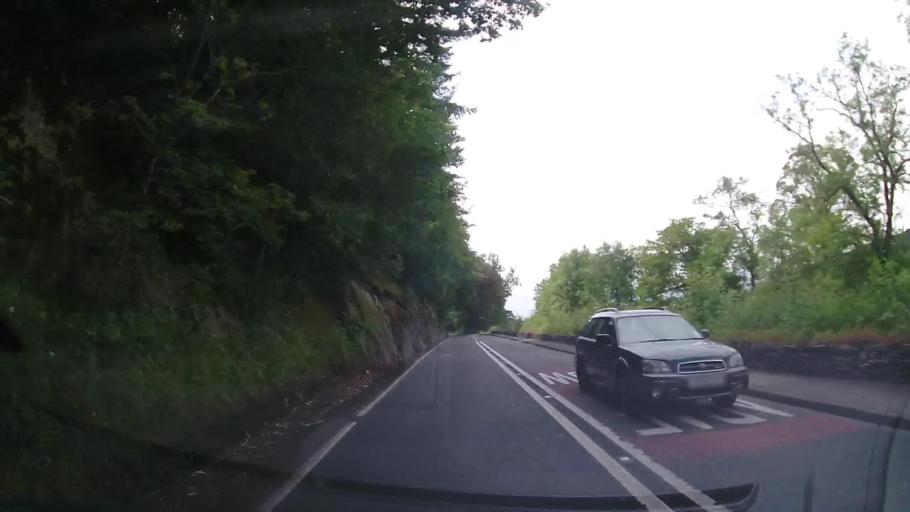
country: GB
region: Wales
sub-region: Denbighshire
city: Corwen
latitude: 52.9789
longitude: -3.3451
